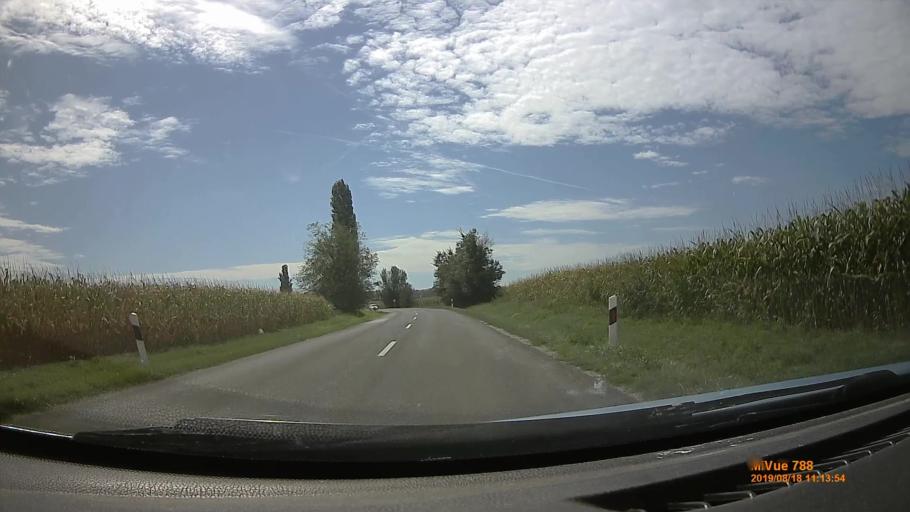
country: HU
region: Fejer
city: Szabadbattyan
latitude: 47.0954
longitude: 18.3906
